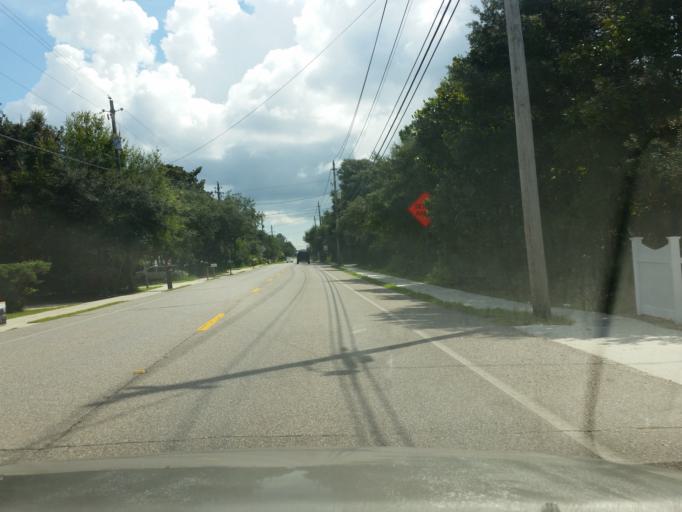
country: US
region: Alabama
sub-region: Baldwin County
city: Orange Beach
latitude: 30.3161
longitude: -87.4389
